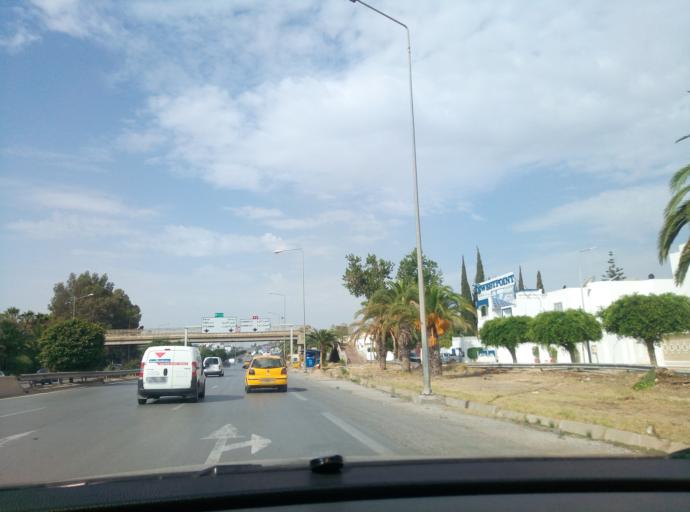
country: TN
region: Tunis
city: Tunis
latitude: 36.8425
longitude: 10.1730
